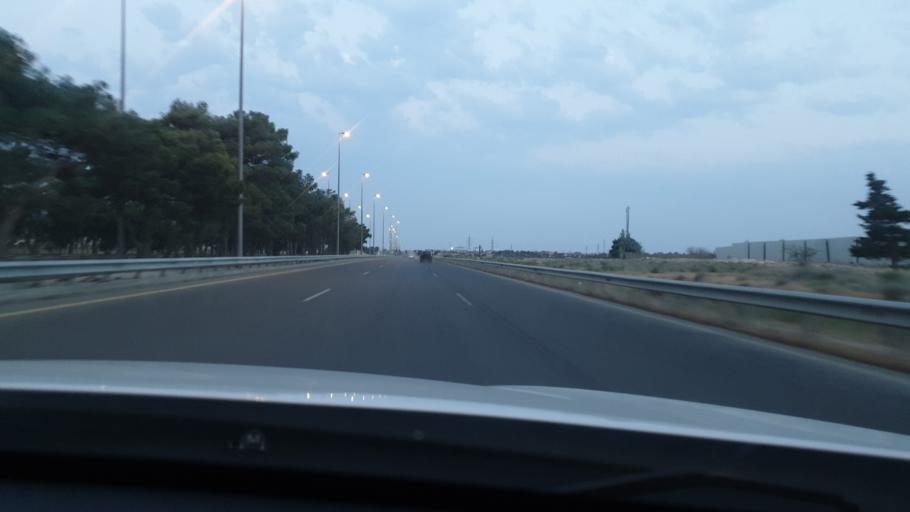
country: AZ
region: Baki
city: Buzovna
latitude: 40.5469
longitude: 50.0826
